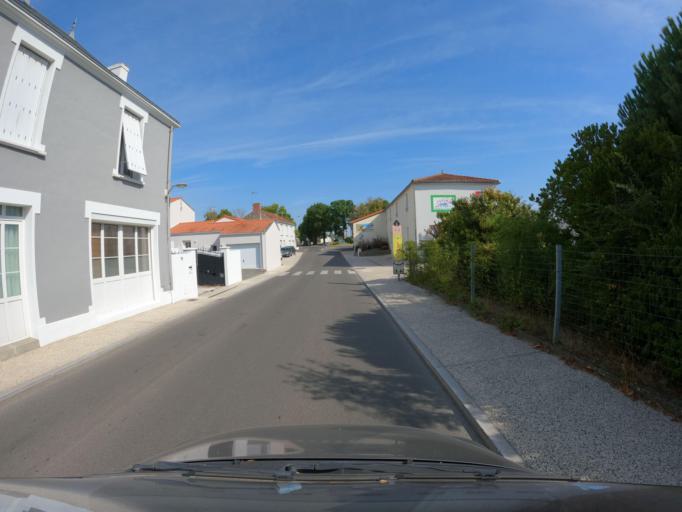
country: FR
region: Pays de la Loire
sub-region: Departement de la Vendee
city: Saint-Christophe-du-Ligneron
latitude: 46.8262
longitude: -1.7615
